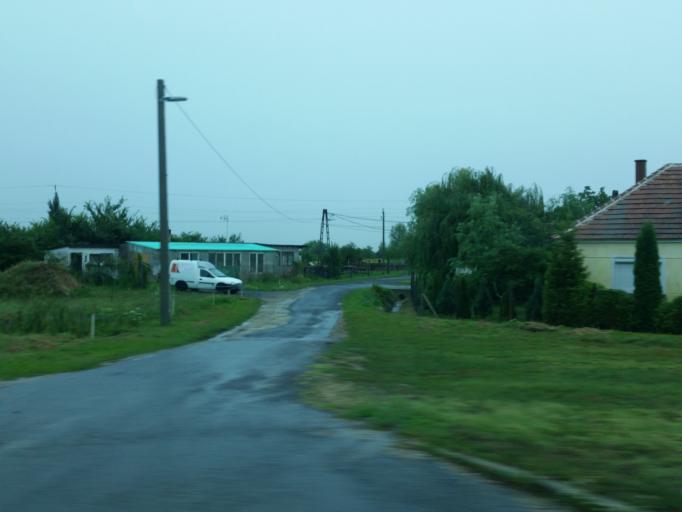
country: HU
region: Vas
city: Sarvar
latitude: 47.3278
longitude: 16.8549
